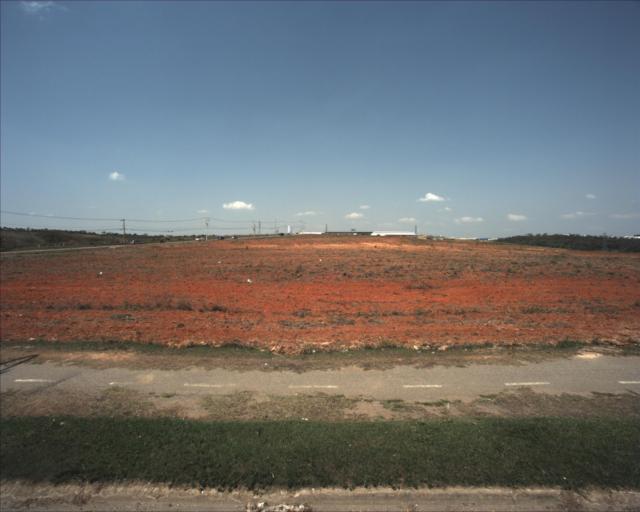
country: BR
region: Sao Paulo
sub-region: Sorocaba
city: Sorocaba
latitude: -23.4294
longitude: -47.4485
